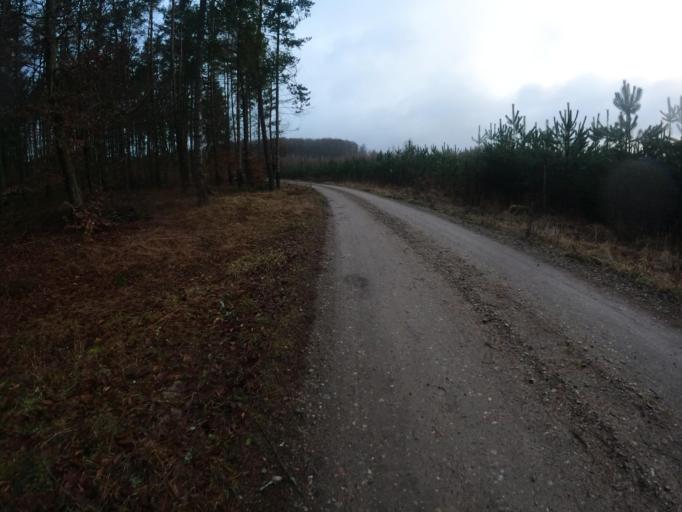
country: PL
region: West Pomeranian Voivodeship
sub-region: Powiat slawienski
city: Slawno
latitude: 54.2811
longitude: 16.7203
